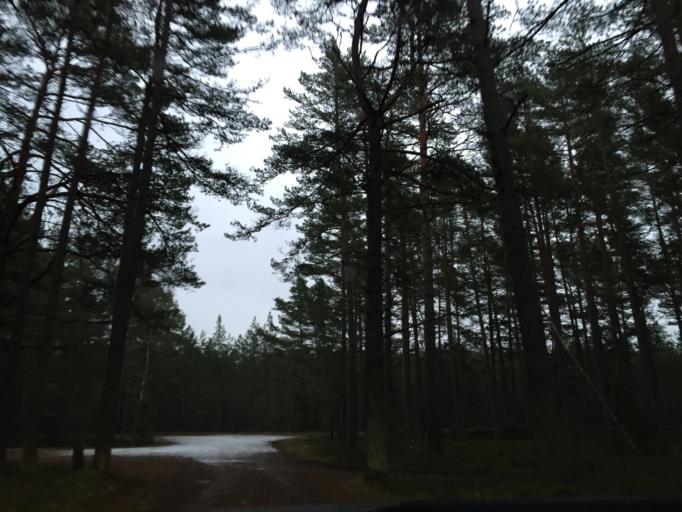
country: EE
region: Saare
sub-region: Kuressaare linn
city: Kuressaare
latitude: 58.5918
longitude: 22.5110
